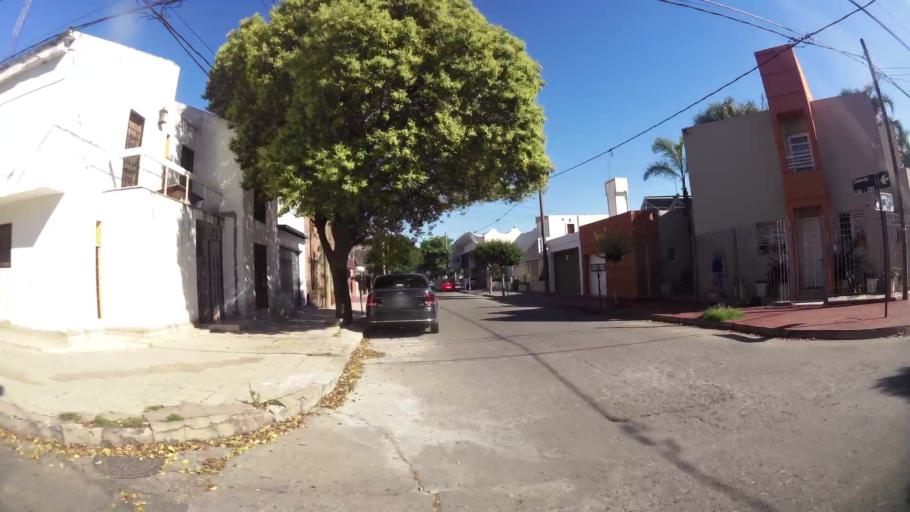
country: AR
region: Cordoba
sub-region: Departamento de Capital
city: Cordoba
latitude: -31.4344
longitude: -64.1586
